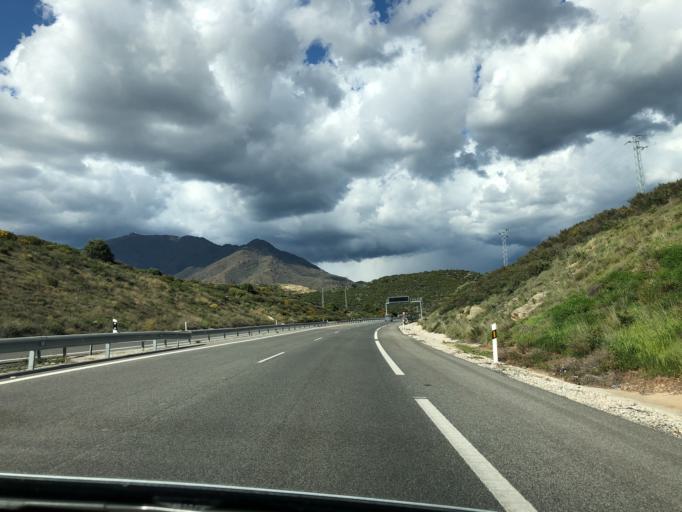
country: ES
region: Andalusia
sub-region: Provincia de Malaga
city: Manilva
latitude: 36.4189
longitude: -5.2197
